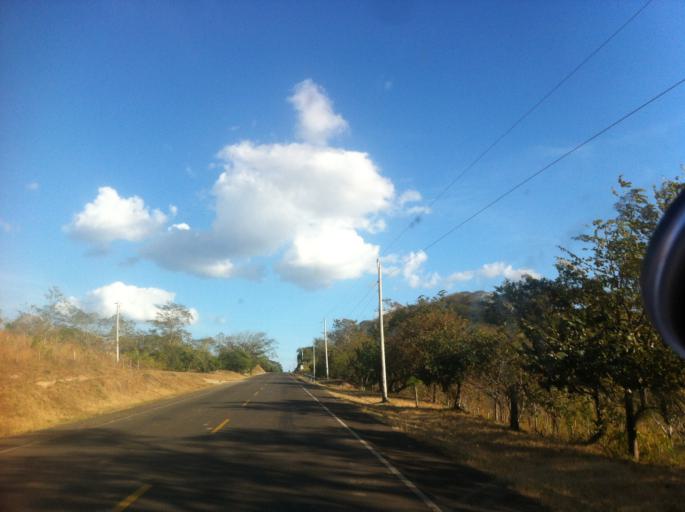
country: NI
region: Chontales
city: Acoyapa
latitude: 11.8586
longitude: -85.0613
